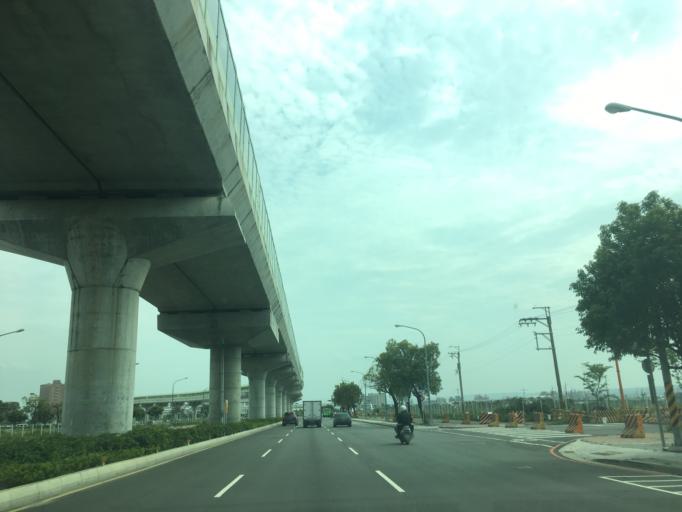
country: TW
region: Taiwan
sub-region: Taichung City
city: Taichung
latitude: 24.1284
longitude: 120.6463
